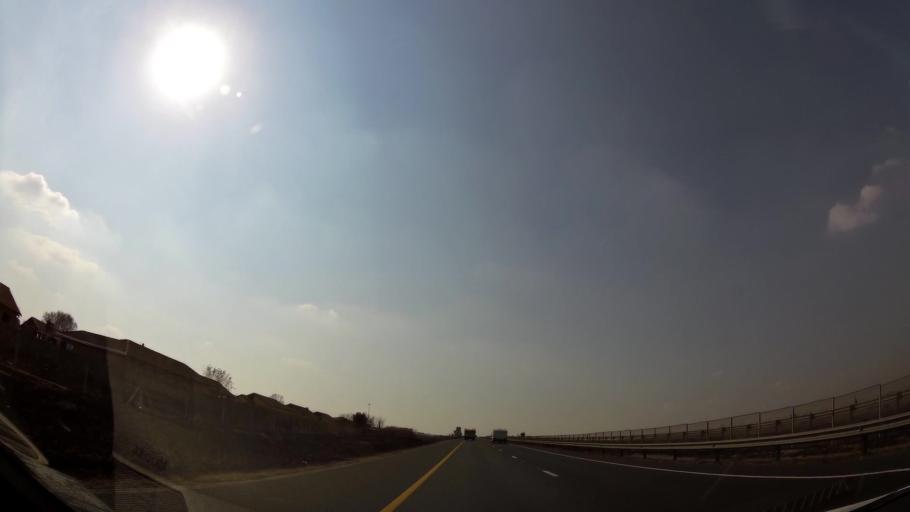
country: ZA
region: Gauteng
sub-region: Ekurhuleni Metropolitan Municipality
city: Brakpan
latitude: -26.1614
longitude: 28.4128
